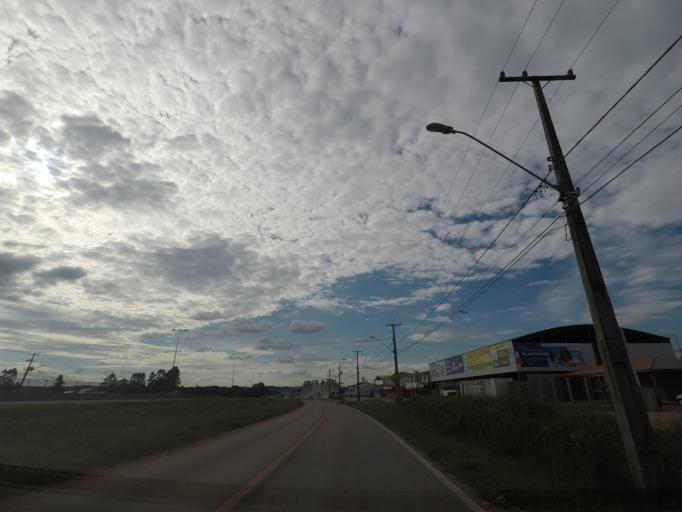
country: BR
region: Parana
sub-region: Araucaria
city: Araucaria
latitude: -25.6319
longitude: -49.3132
